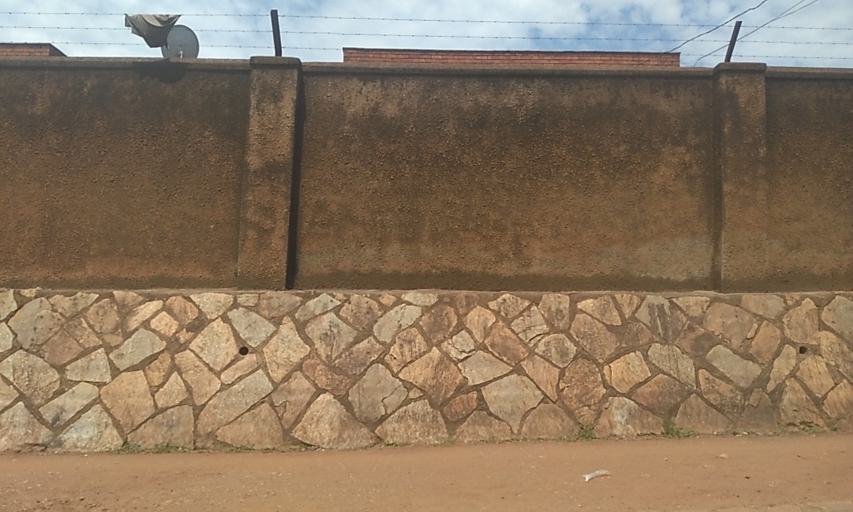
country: UG
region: Central Region
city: Kampala Central Division
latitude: 0.3114
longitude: 32.5655
